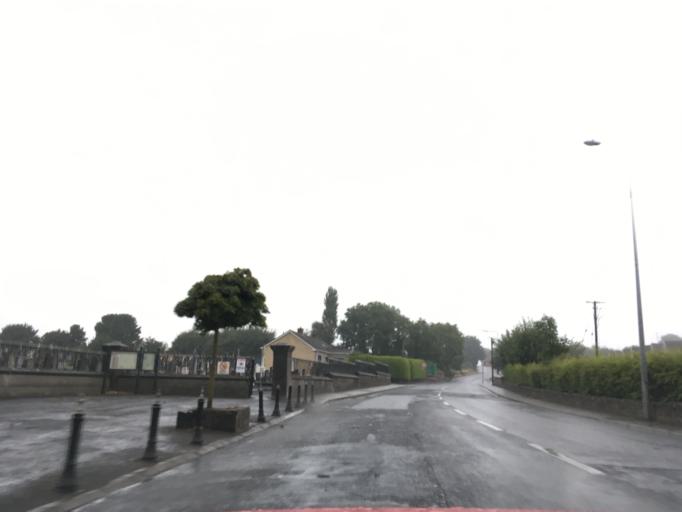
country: IE
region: Munster
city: Tipperary
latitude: 52.4763
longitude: -8.1452
